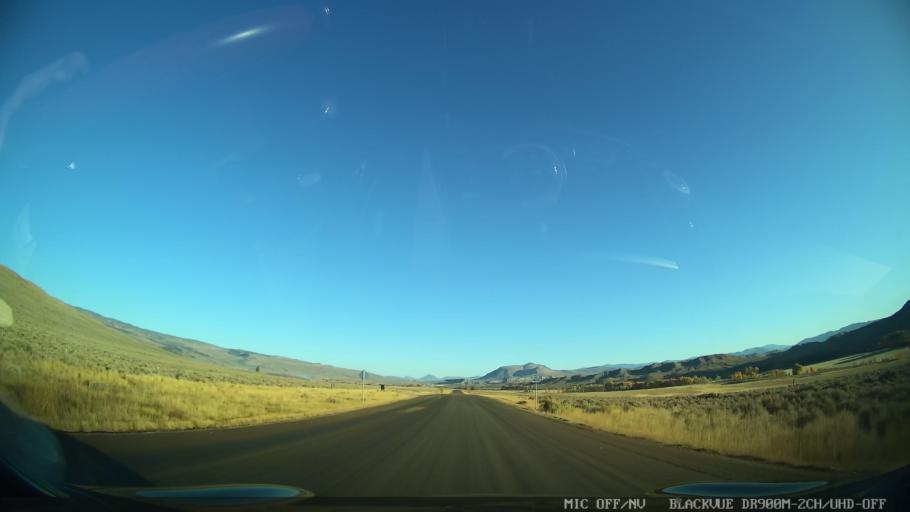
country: US
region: Colorado
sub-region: Grand County
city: Kremmling
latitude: 40.0194
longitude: -106.3888
